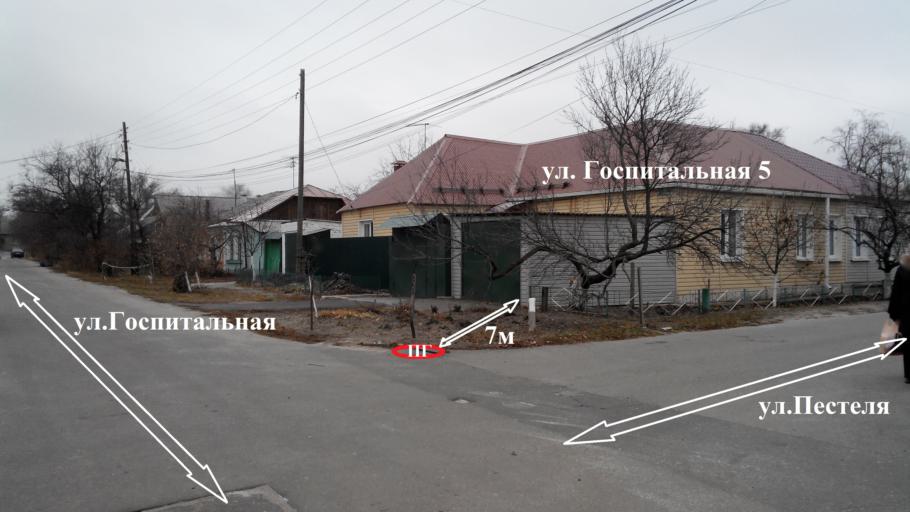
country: RU
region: Voronezj
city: Voronezh
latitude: 51.6436
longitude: 39.1748
